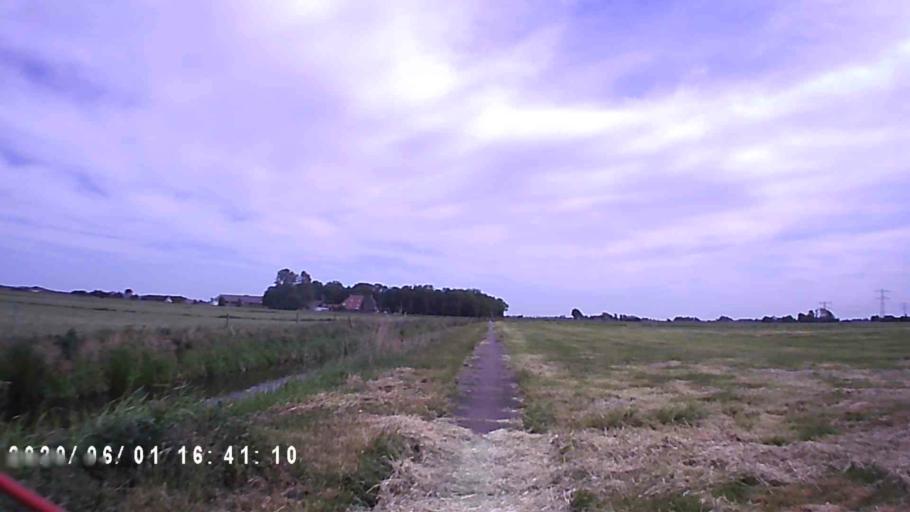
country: NL
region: Friesland
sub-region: Gemeente Boarnsterhim
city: Warten
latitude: 53.1850
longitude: 5.8776
